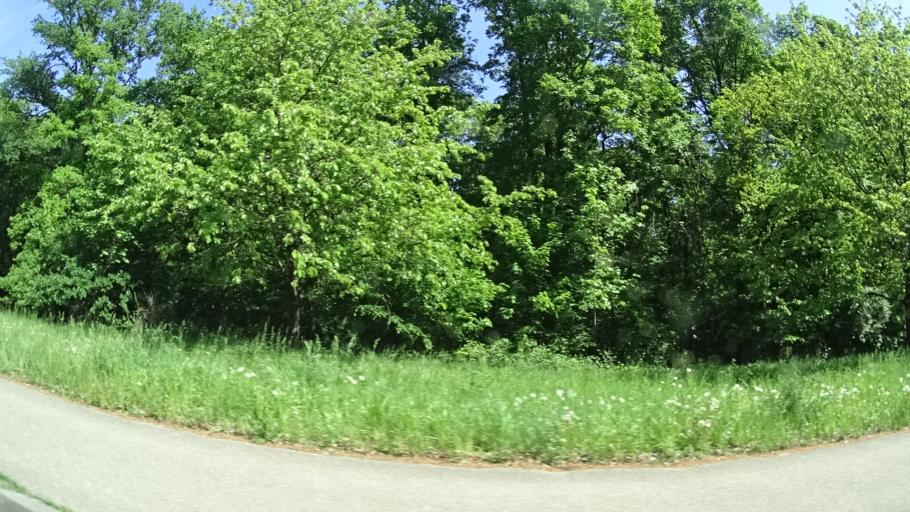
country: DE
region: Baden-Wuerttemberg
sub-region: Karlsruhe Region
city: Ettlingen
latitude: 48.9377
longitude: 8.3722
